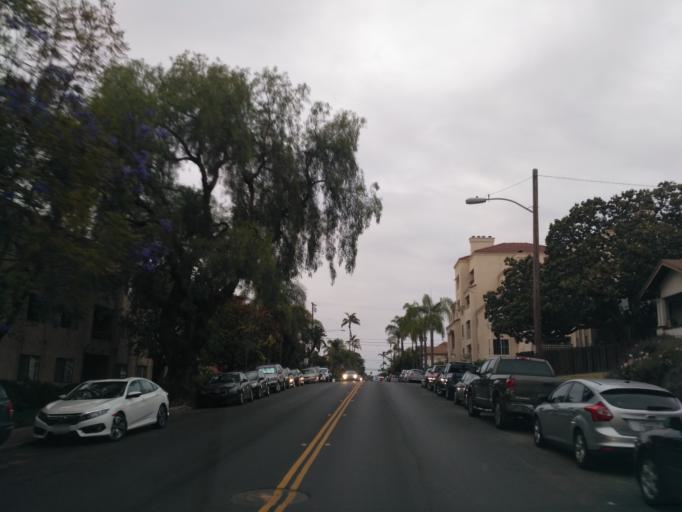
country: US
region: California
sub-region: San Diego County
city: San Diego
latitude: 32.7441
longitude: -117.1639
